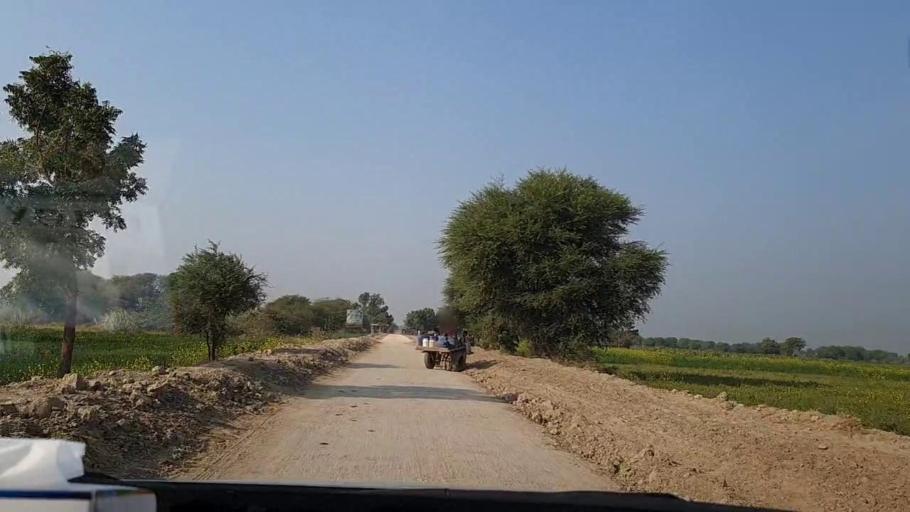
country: PK
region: Sindh
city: Tando Ghulam Ali
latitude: 25.1759
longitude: 68.8767
